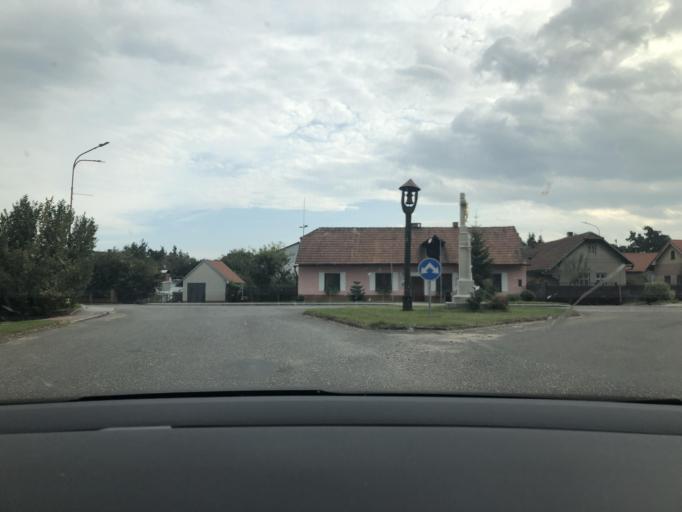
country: CZ
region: Pardubicky
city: Chvaletice
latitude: 50.0803
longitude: 15.4453
